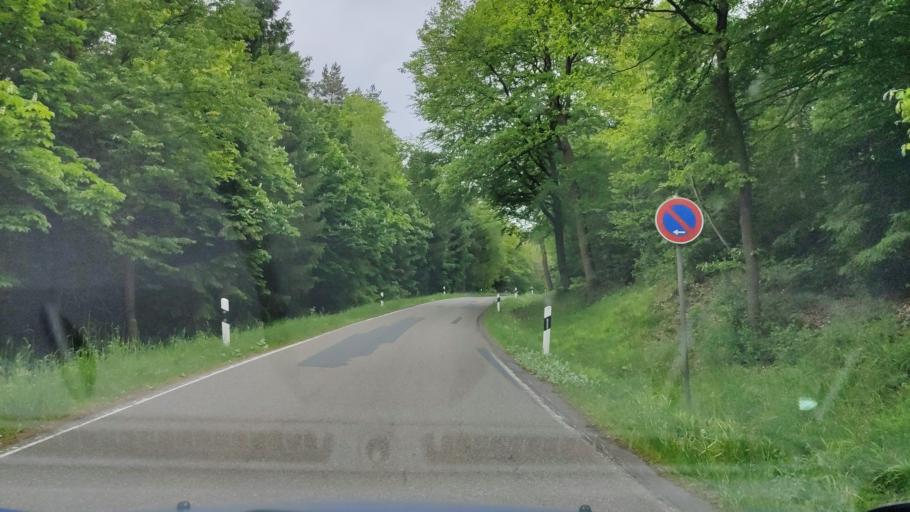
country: DE
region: Lower Saxony
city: Dassel
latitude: 51.7081
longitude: 9.7328
